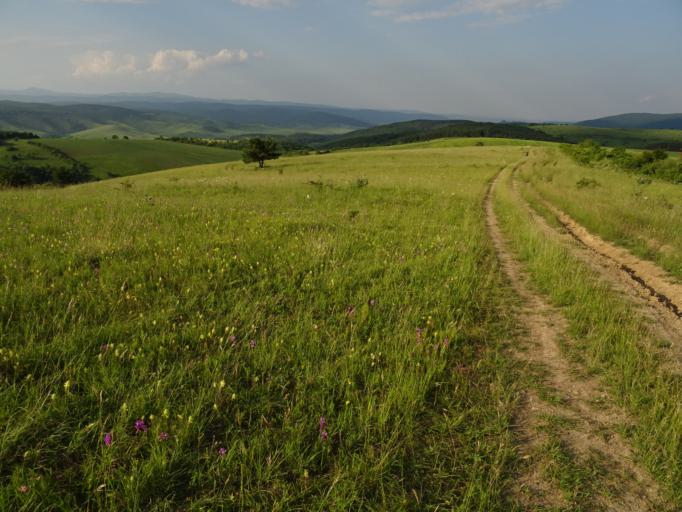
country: HU
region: Borsod-Abauj-Zemplen
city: Rudabanya
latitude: 48.4667
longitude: 20.6378
